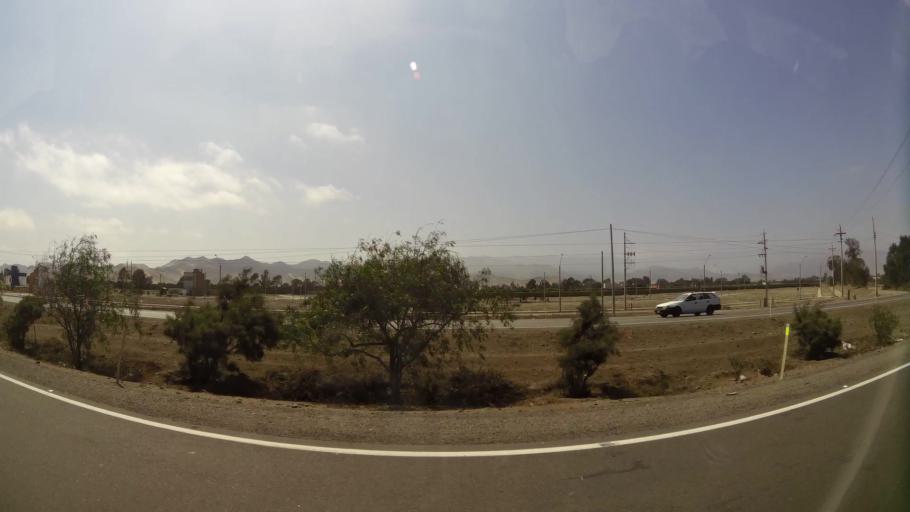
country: PE
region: Lima
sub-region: Provincia de Canete
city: Asia
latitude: -12.7810
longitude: -76.5824
